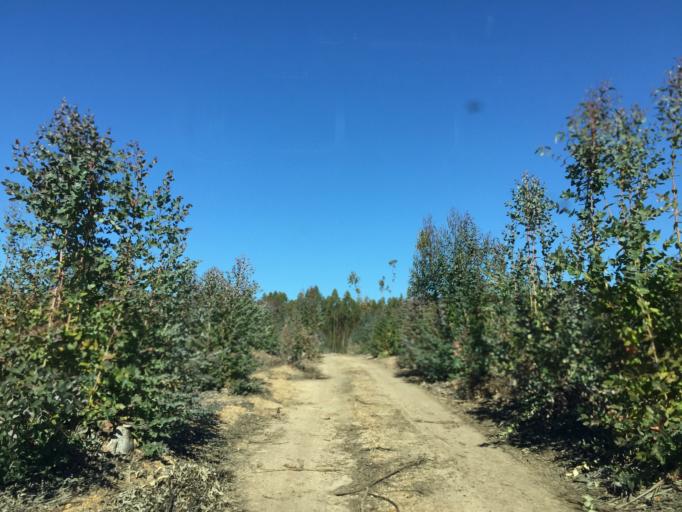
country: PT
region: Portalegre
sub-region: Nisa
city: Nisa
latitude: 39.4962
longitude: -7.7734
